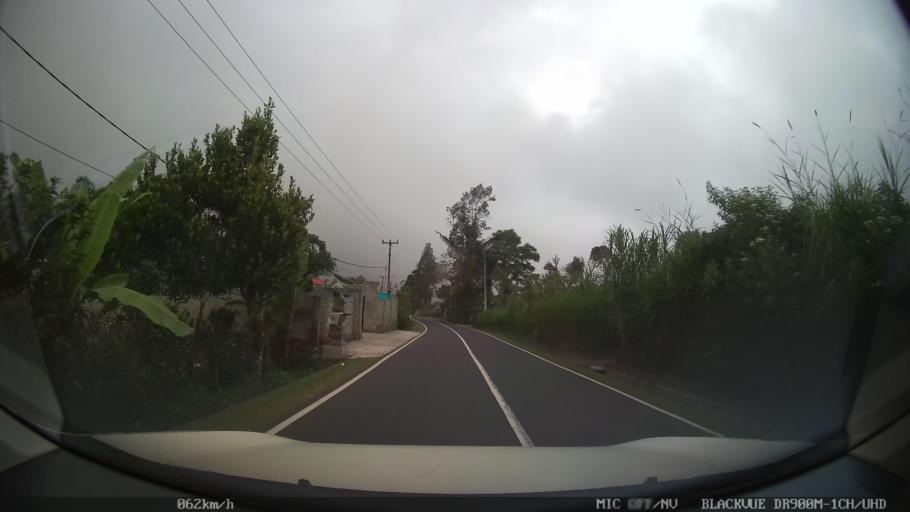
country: ID
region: Bali
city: Banjar Kedisan
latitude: -8.2832
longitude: 115.3209
